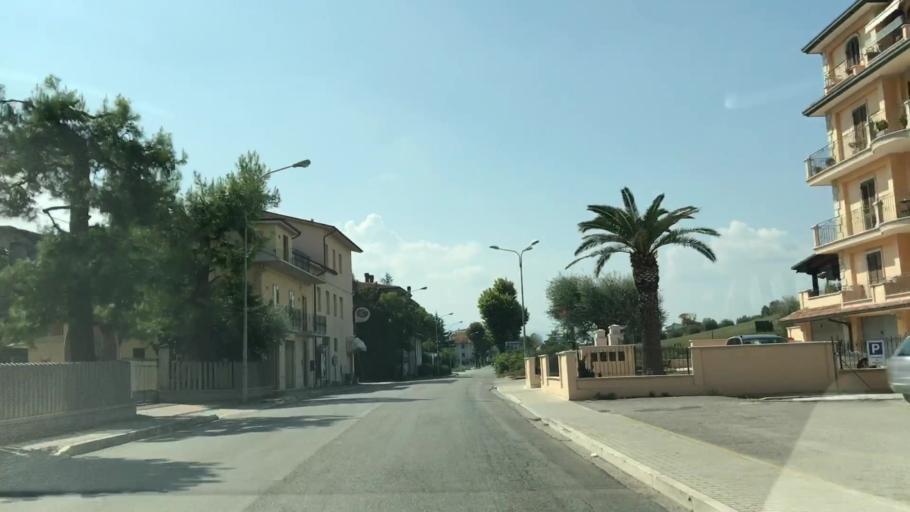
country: IT
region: The Marches
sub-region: Provincia di Ascoli Piceno
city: Stella
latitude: 42.8861
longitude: 13.8072
